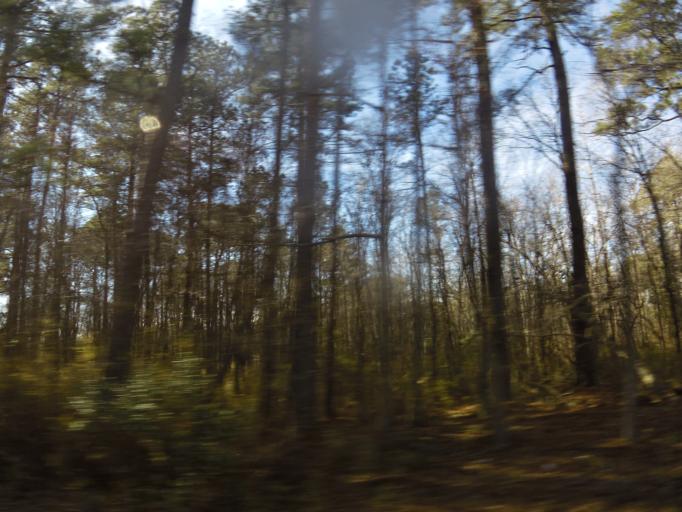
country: US
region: Virginia
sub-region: Isle of Wight County
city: Windsor
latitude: 36.8326
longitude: -76.7463
